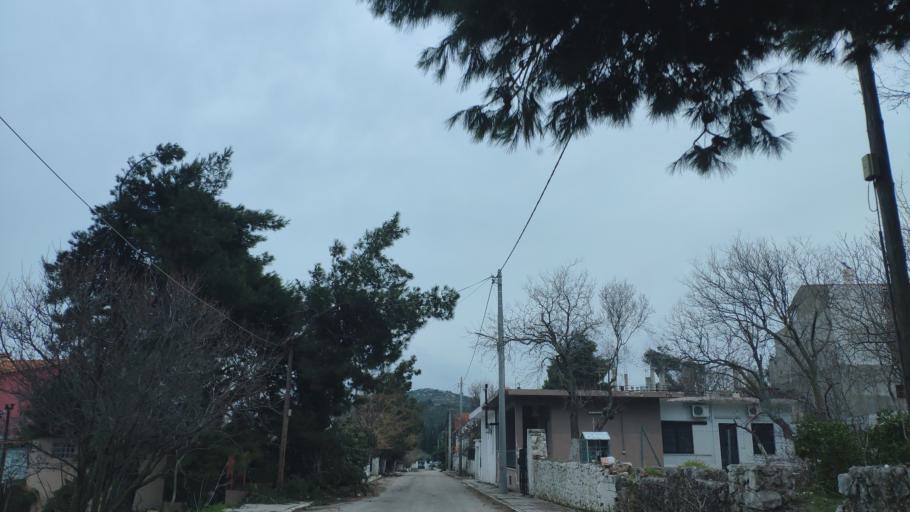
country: GR
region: Attica
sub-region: Nomarchia Dytikis Attikis
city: Vilia
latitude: 38.1663
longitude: 23.3397
